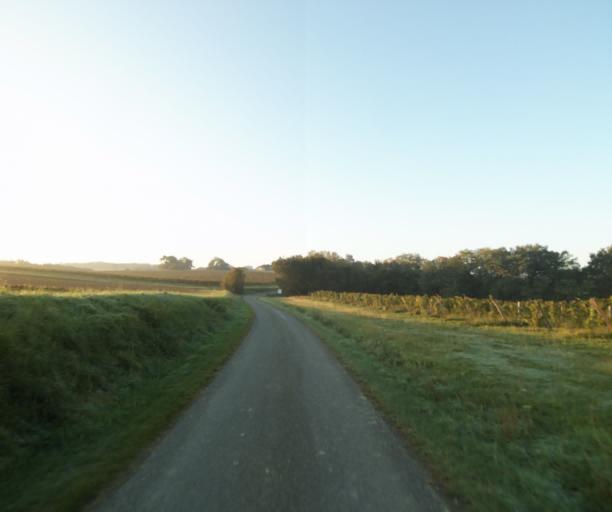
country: FR
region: Midi-Pyrenees
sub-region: Departement du Gers
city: Eauze
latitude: 43.7932
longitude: 0.1703
